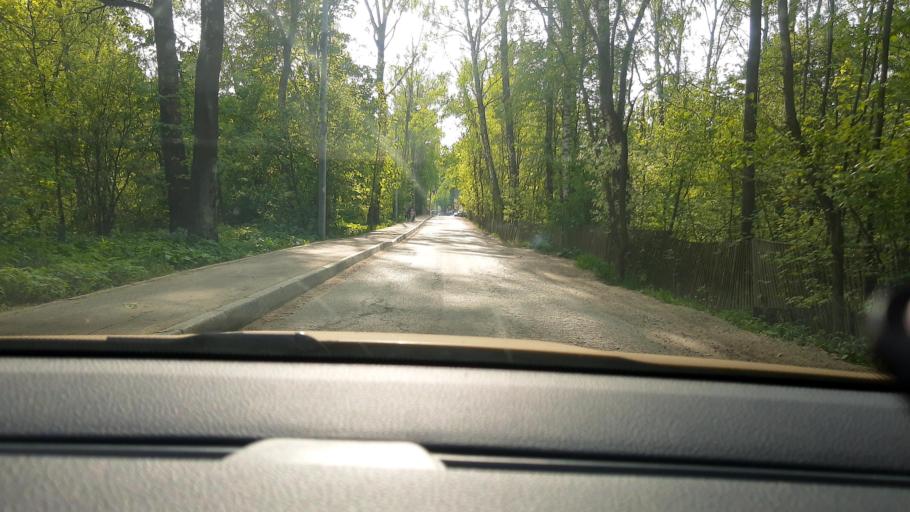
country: RU
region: Moskovskaya
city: Sheremet'yevskiy
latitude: 55.9548
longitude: 37.4460
